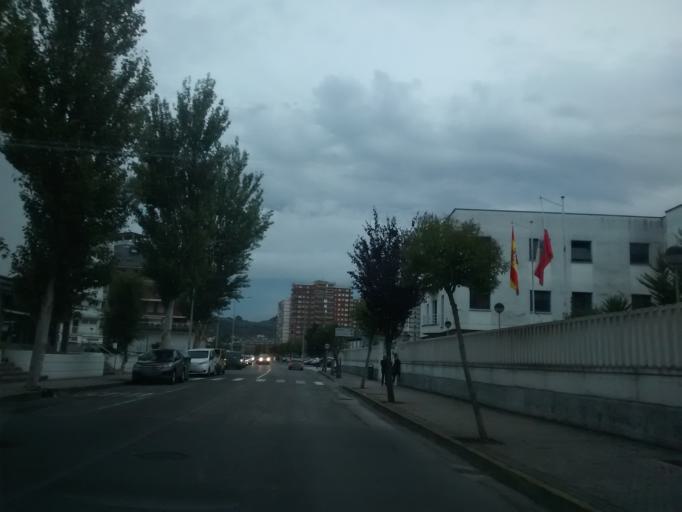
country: ES
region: Cantabria
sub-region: Provincia de Cantabria
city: Colindres
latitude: 43.4142
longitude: -3.4412
